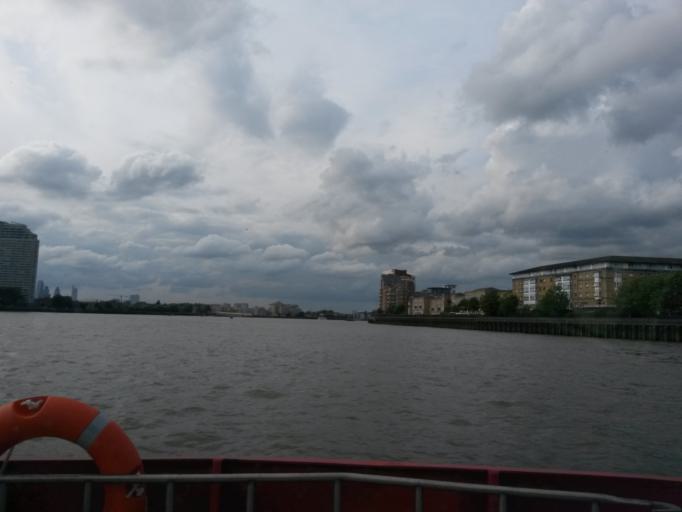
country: GB
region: England
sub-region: Greater London
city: Poplar
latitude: 51.4874
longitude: -0.0235
